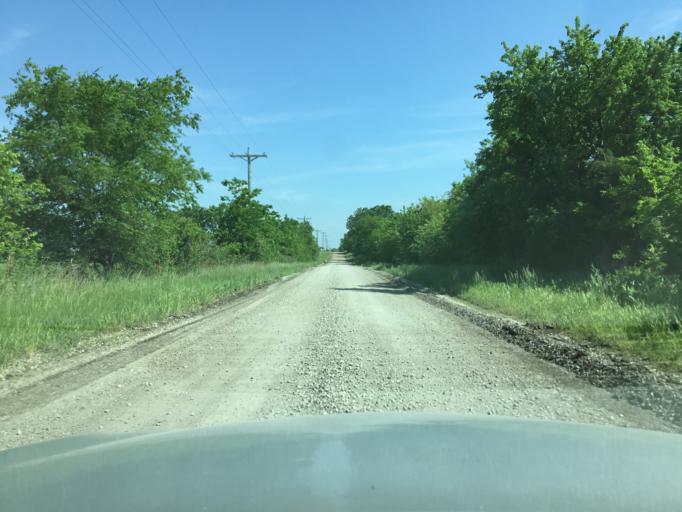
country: US
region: Kansas
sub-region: Labette County
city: Oswego
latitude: 37.1715
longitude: -95.1399
